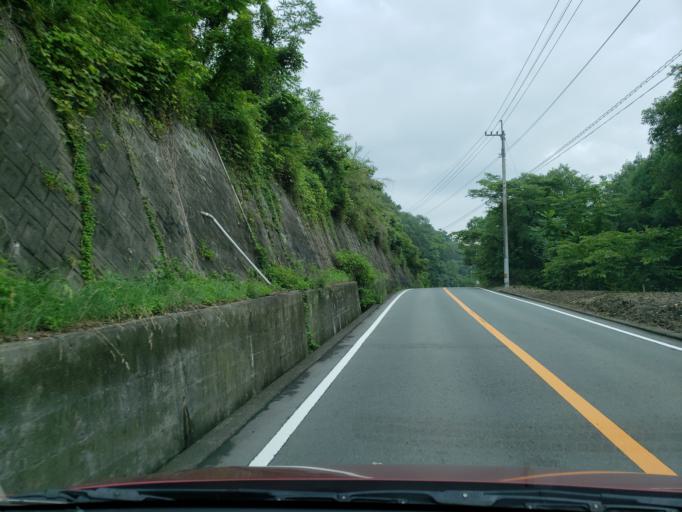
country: JP
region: Tokushima
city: Kamojimacho-jogejima
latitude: 34.1112
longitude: 134.2915
